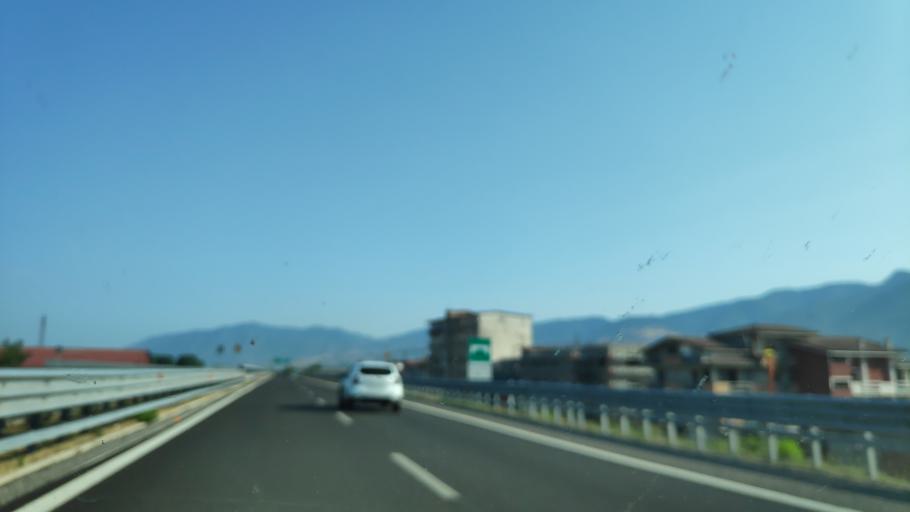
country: IT
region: Campania
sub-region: Provincia di Salerno
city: Buonabitacolo
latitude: 40.2934
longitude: 15.6486
